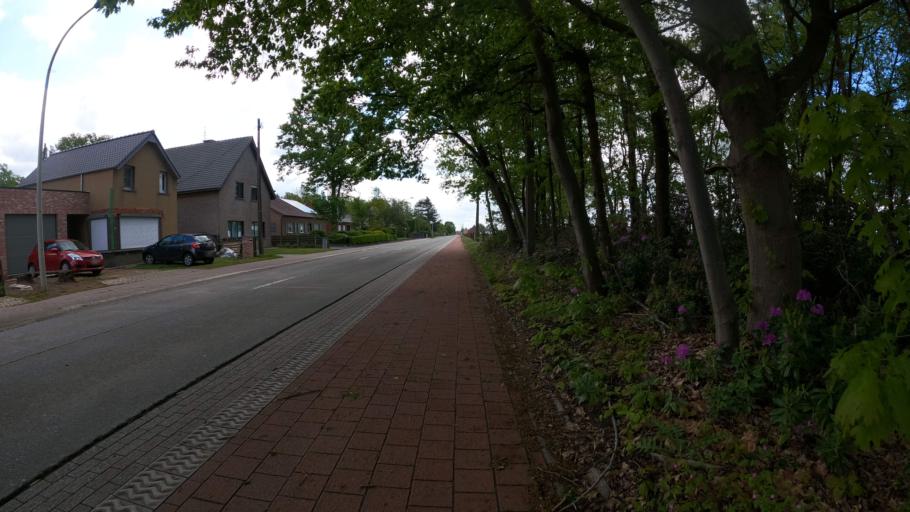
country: BE
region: Flanders
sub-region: Provincie Antwerpen
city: Rijkevorsel
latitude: 51.3130
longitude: 4.7770
